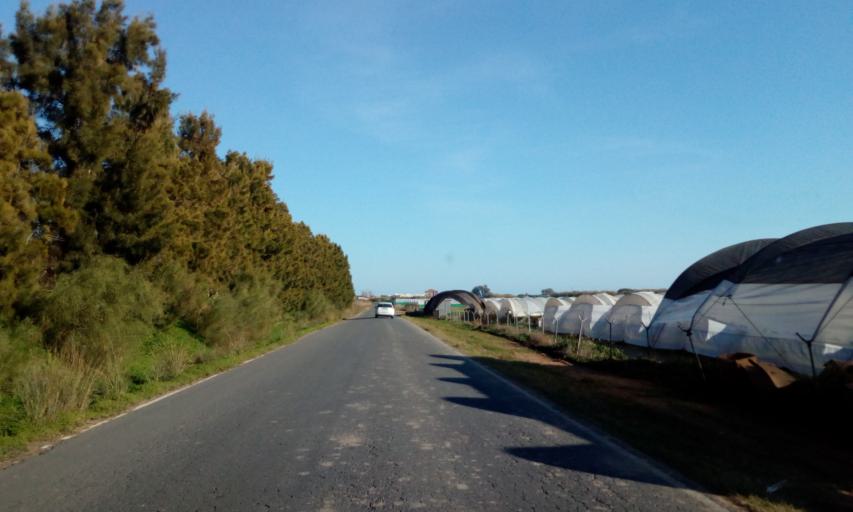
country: ES
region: Andalusia
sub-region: Provincia de Huelva
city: Isla Cristina
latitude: 37.2092
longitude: -7.2635
